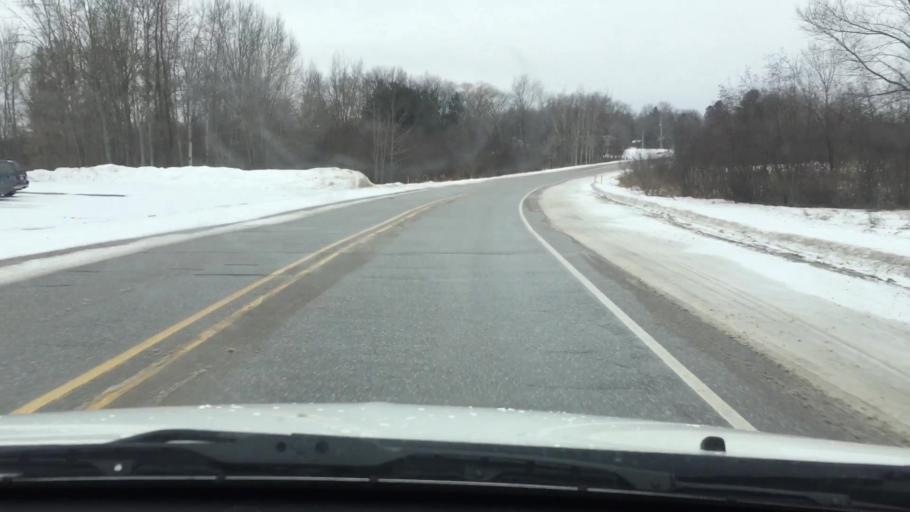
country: US
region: Michigan
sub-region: Osceola County
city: Reed City
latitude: 44.0414
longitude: -85.4448
